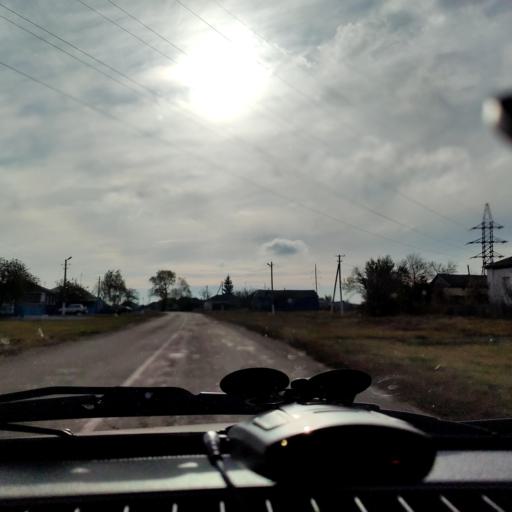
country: RU
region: Voronezj
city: Rossosh'
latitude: 51.2088
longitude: 38.7616
